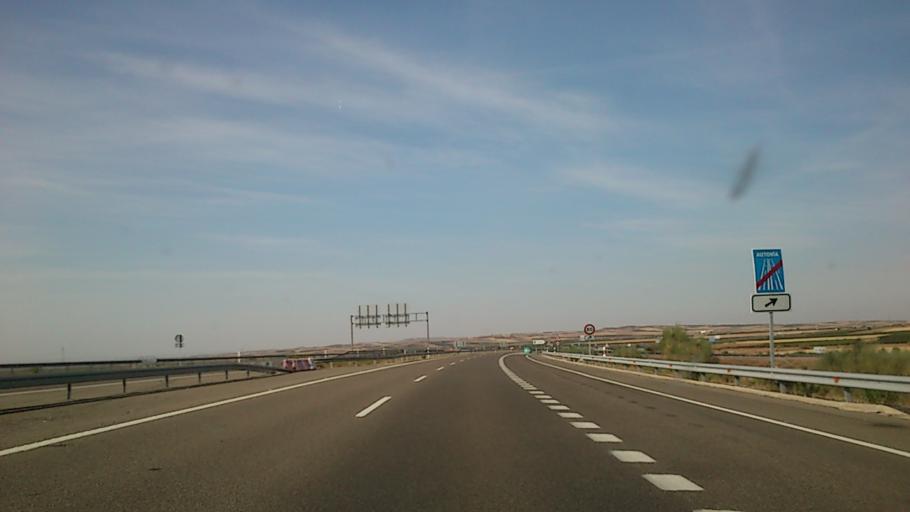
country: ES
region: Aragon
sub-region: Provincia de Zaragoza
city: Carinena
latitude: 41.3671
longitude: -1.2028
